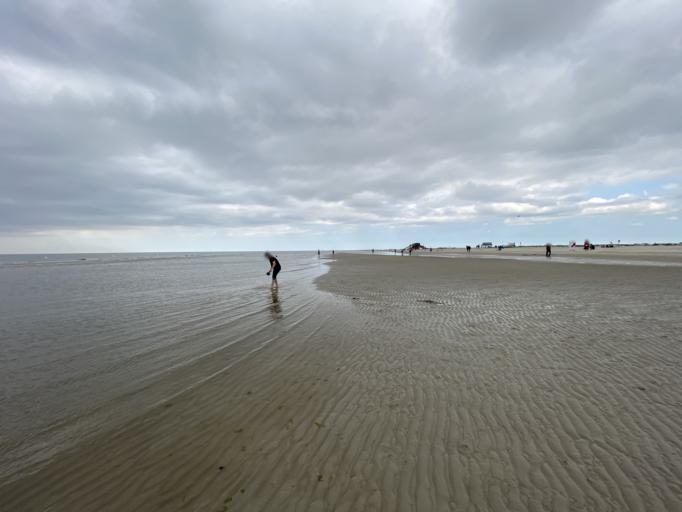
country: DE
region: Schleswig-Holstein
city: Sankt Peter-Ording
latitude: 54.3316
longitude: 8.5881
